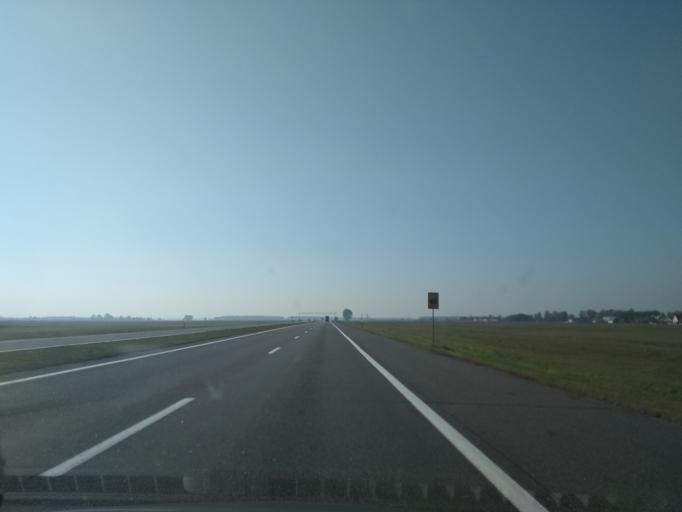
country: BY
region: Brest
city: Byaroza
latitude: 52.4346
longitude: 24.8583
